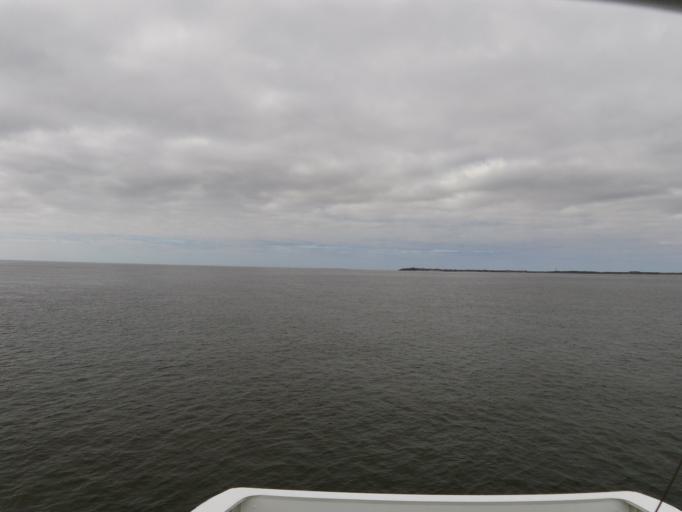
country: DE
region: Schleswig-Holstein
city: Witsum
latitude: 54.6424
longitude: 8.4513
